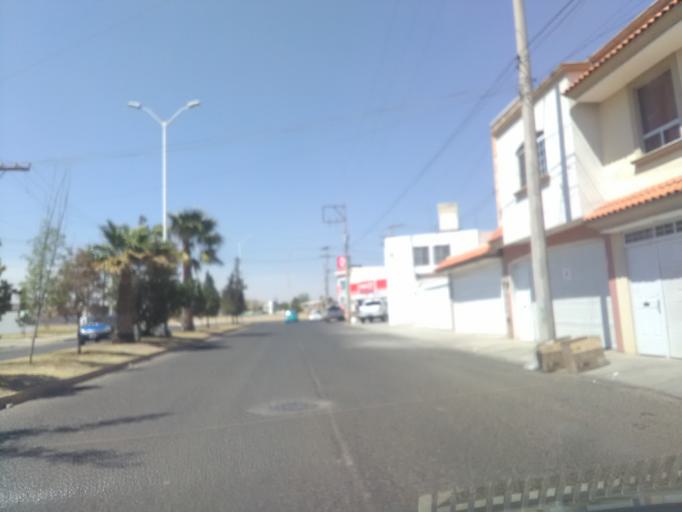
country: MX
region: Durango
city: Victoria de Durango
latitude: 24.0401
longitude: -104.6503
